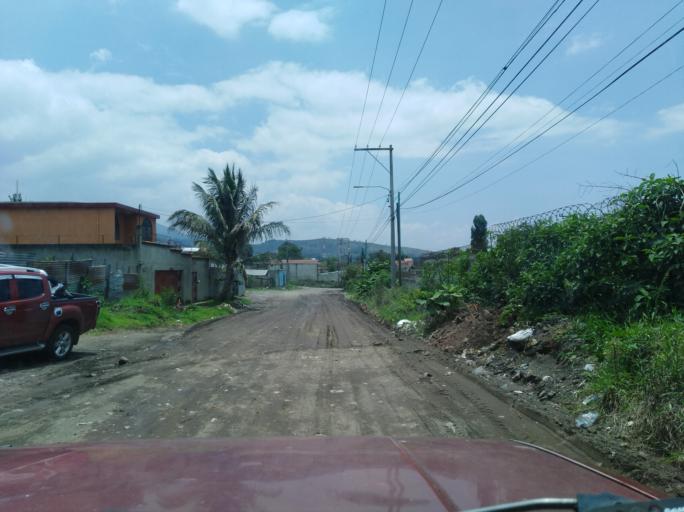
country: GT
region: Guatemala
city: Villa Nueva
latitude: 14.5264
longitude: -90.6190
